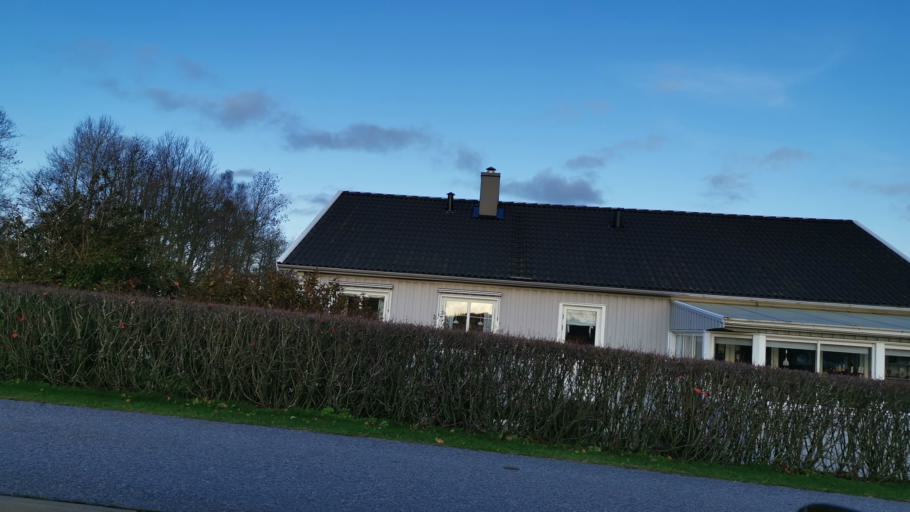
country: SE
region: Vaestra Goetaland
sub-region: Munkedals Kommun
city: Munkedal
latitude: 58.4659
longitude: 11.6615
